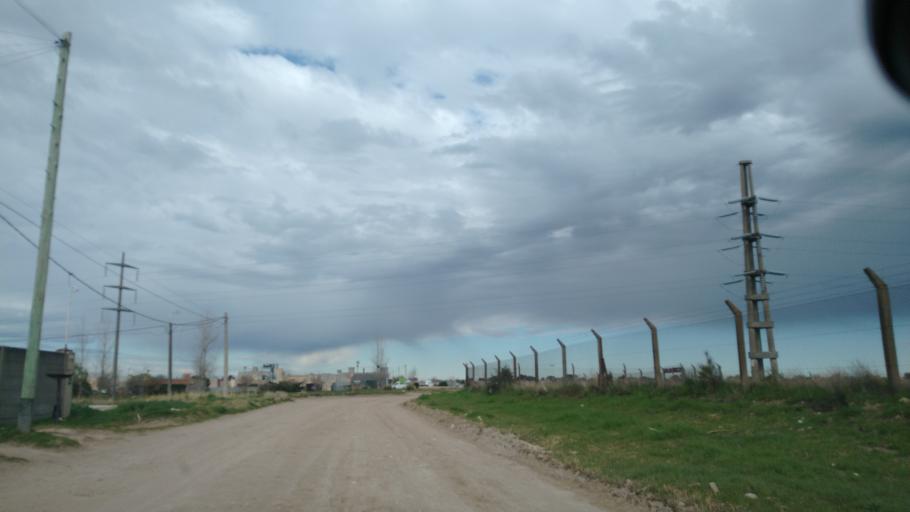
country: AR
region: Buenos Aires
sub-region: Partido de Bahia Blanca
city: Bahia Blanca
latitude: -38.7045
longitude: -62.2085
